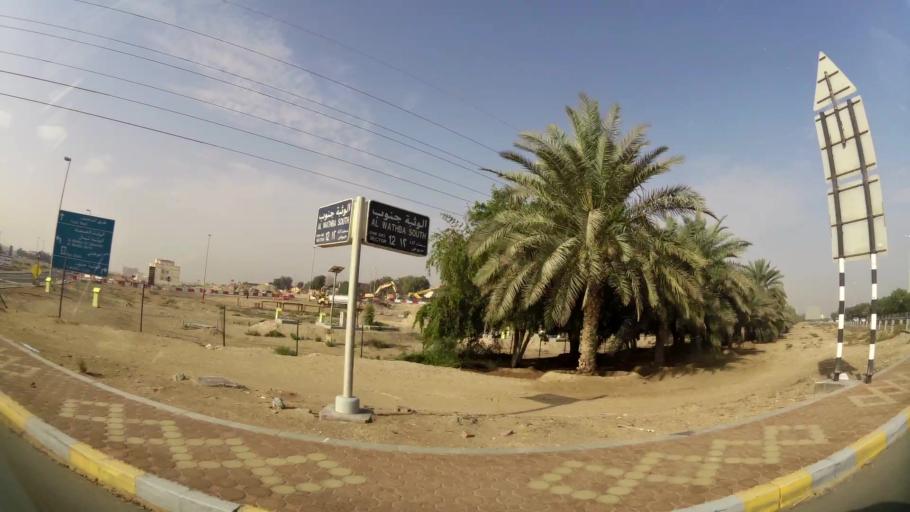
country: AE
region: Abu Dhabi
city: Abu Dhabi
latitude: 24.2691
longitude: 54.6653
